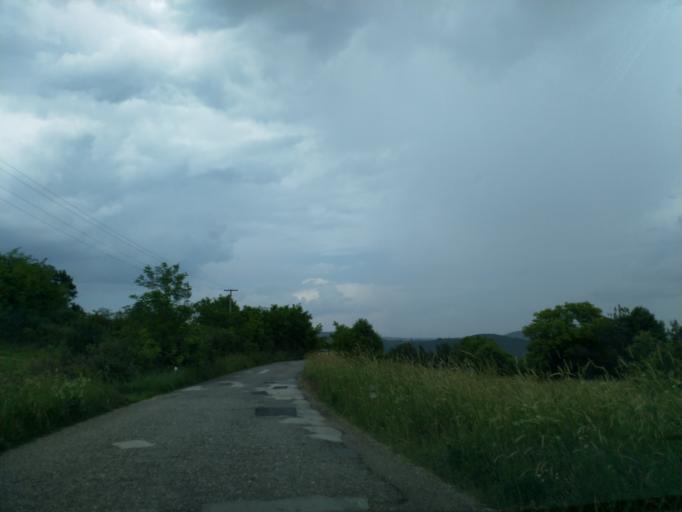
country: RS
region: Central Serbia
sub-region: Borski Okrug
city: Bor
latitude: 43.9908
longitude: 21.9755
